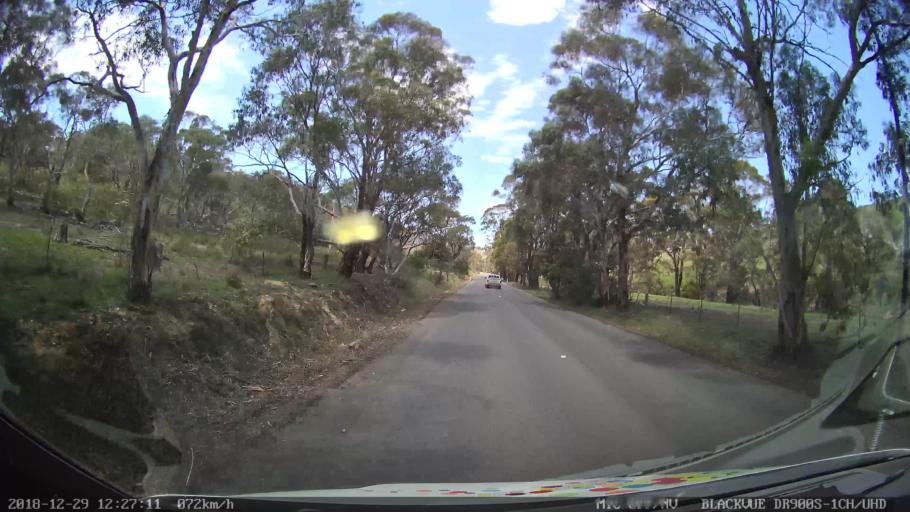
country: AU
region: Australian Capital Territory
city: Macarthur
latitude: -35.4739
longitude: 149.2232
